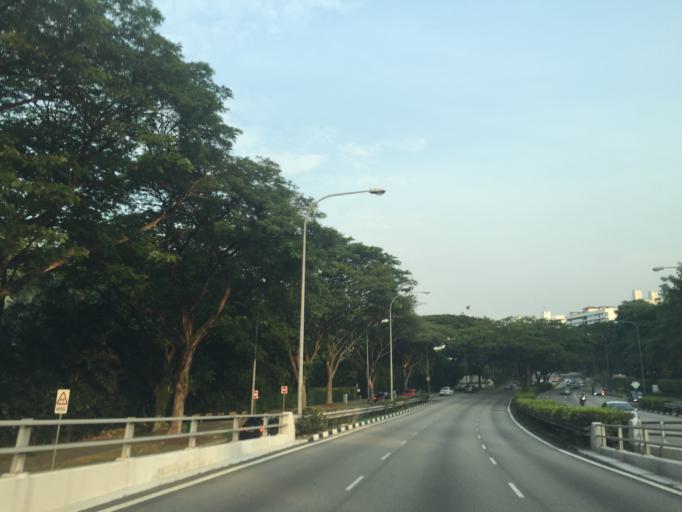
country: SG
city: Singapore
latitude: 1.3114
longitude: 103.8012
